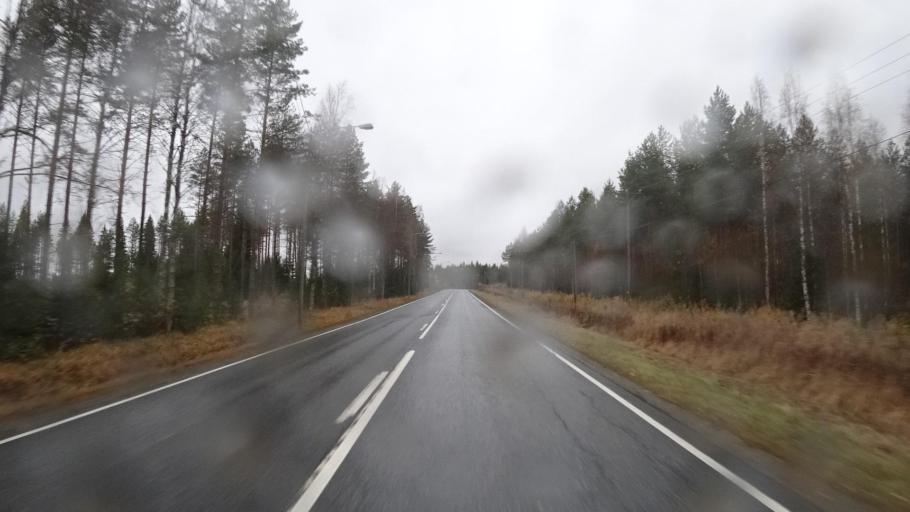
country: FI
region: Northern Savo
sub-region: Koillis-Savo
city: Tuusniemi
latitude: 62.8723
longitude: 28.3222
